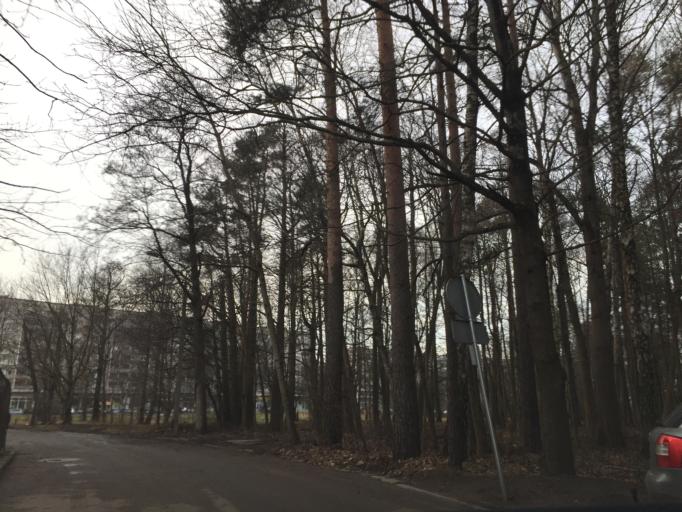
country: LV
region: Marupe
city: Marupe
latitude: 56.9548
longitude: 24.0112
